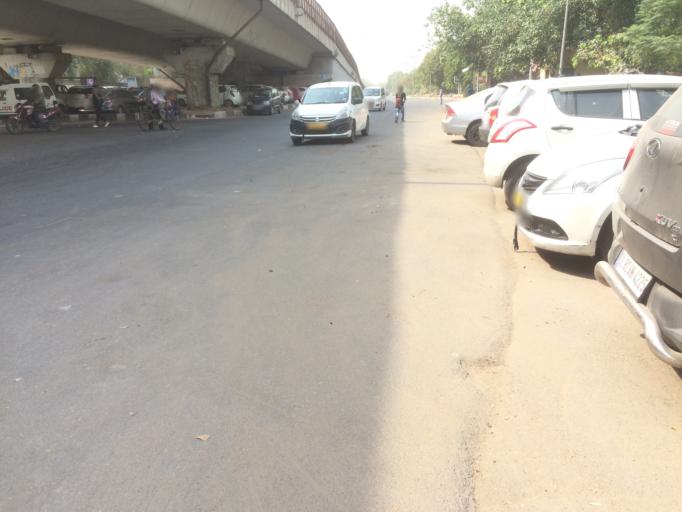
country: IN
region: NCT
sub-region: Central Delhi
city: Karol Bagh
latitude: 28.6192
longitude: 77.1362
